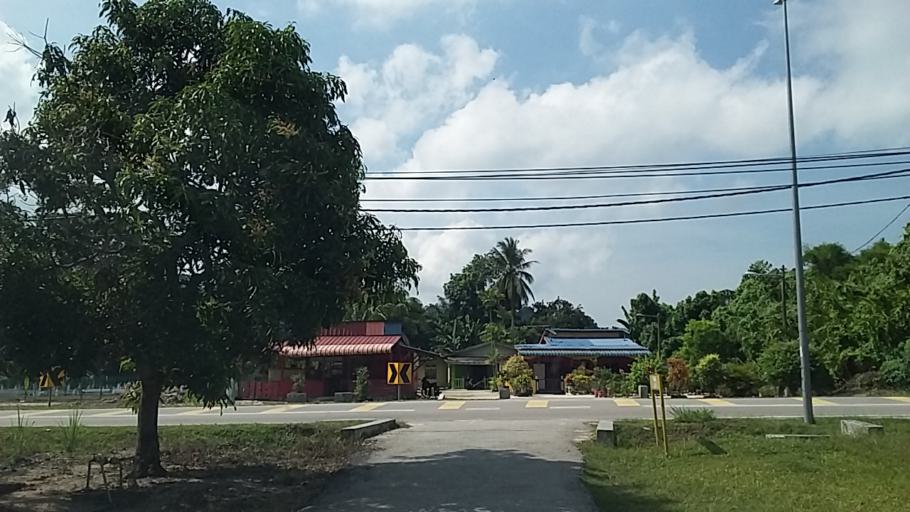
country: MY
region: Johor
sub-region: Daerah Batu Pahat
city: Batu Pahat
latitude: 1.7939
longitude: 102.8968
